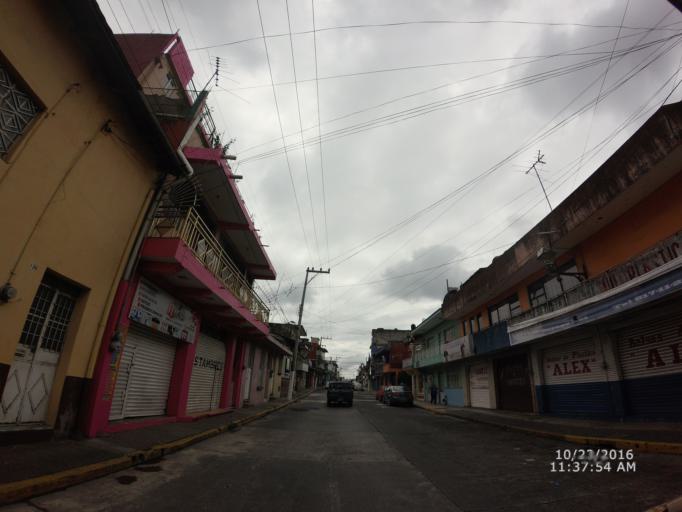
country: MX
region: Veracruz
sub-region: Xalapa
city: Xalapa de Enriquez
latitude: 19.5339
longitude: -96.9275
